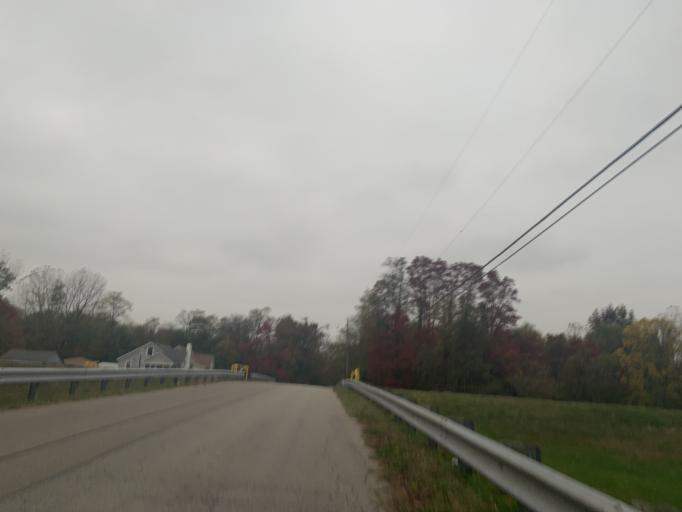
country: US
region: Kentucky
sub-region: Jefferson County
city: Saint Dennis
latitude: 38.2070
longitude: -85.8563
